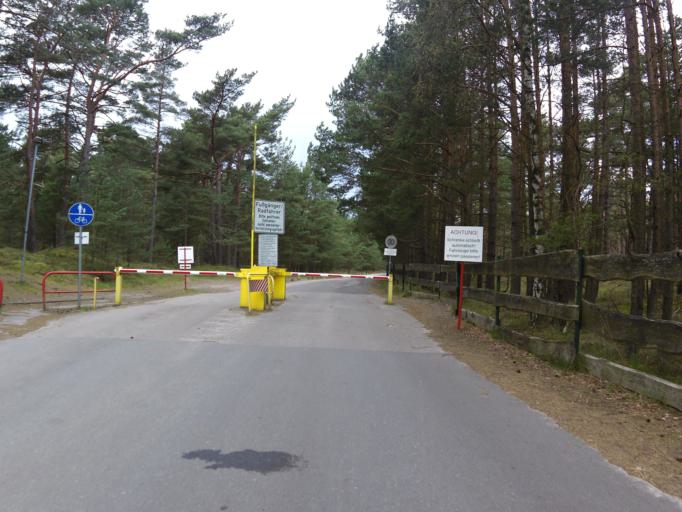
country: DE
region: Mecklenburg-Vorpommern
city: Ostseebad Prerow
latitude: 54.4545
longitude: 12.5464
